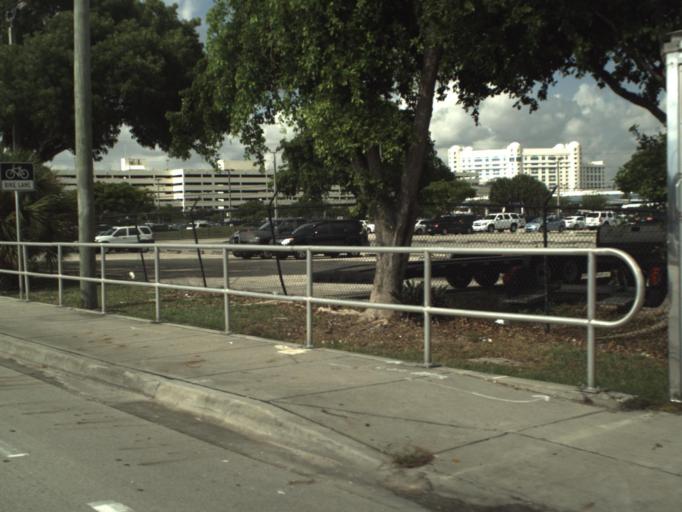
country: US
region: Florida
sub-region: Broward County
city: Davie
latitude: 26.0571
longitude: -80.2078
